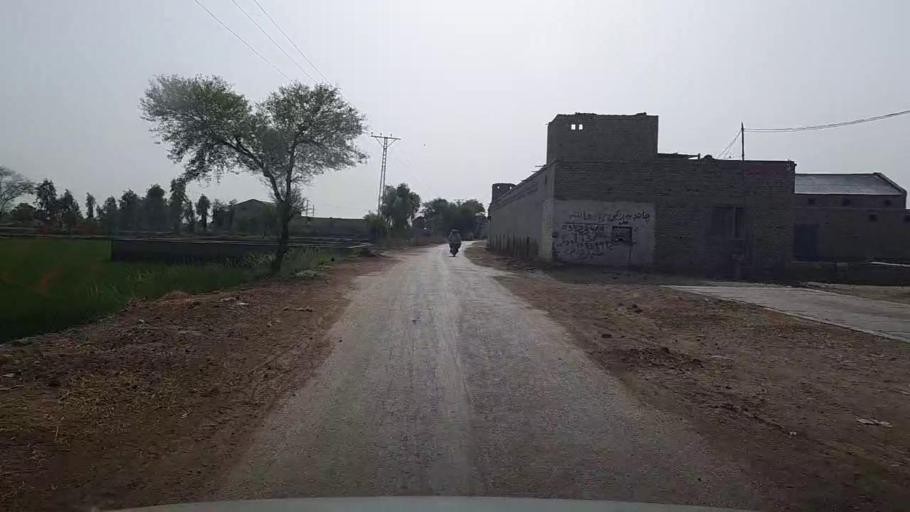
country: PK
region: Sindh
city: Mehar
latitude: 27.1208
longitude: 67.8200
